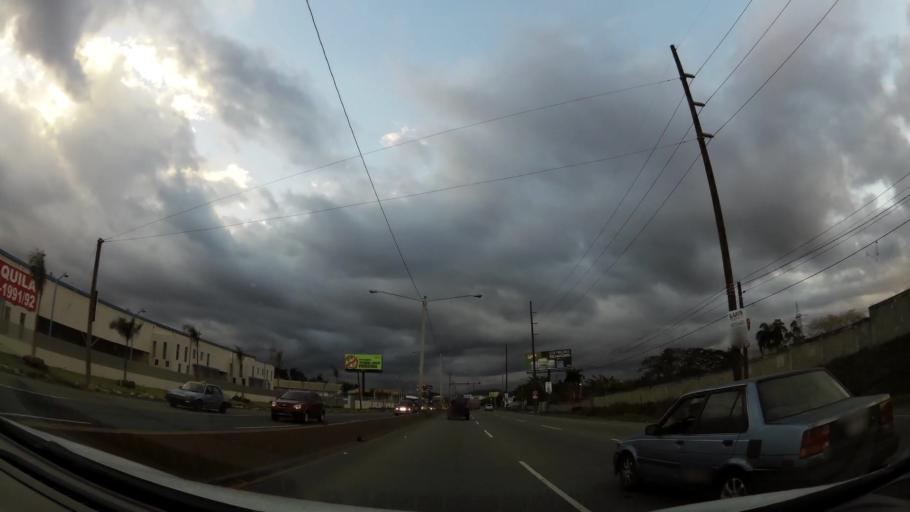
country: DO
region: Santo Domingo
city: Santo Domingo Oeste
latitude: 18.5526
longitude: -70.0550
